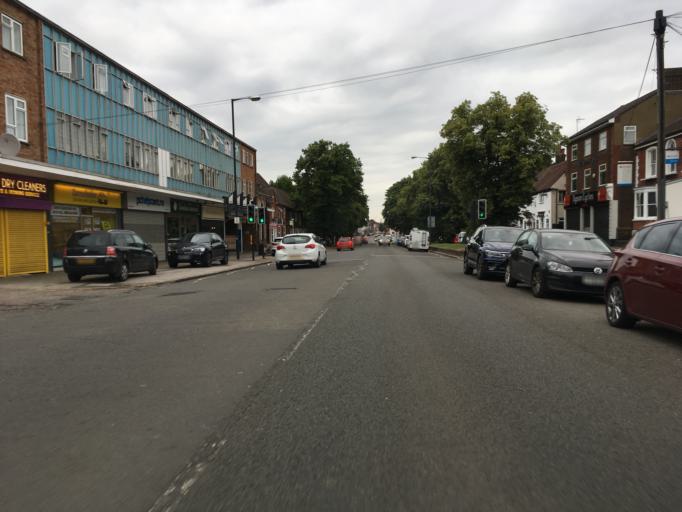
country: GB
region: England
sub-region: Central Bedfordshire
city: Dunstable
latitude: 51.8831
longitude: -0.5165
